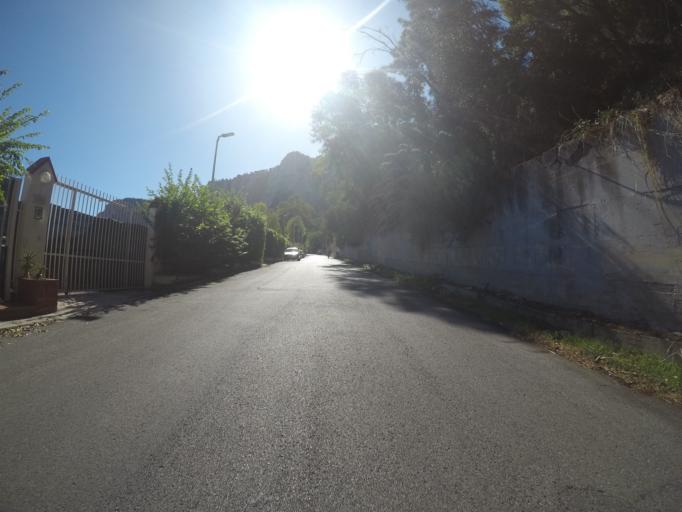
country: IT
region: Sicily
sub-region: Palermo
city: Palermo
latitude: 38.1896
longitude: 13.3401
